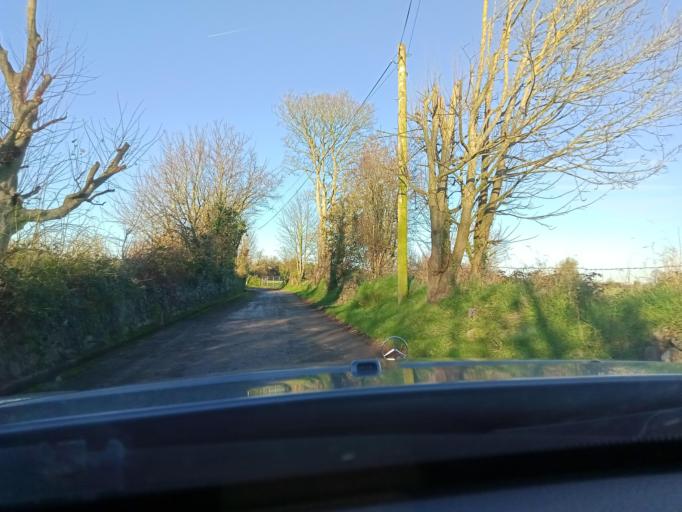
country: IE
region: Leinster
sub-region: Kilkenny
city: Mooncoin
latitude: 52.2927
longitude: -7.2062
